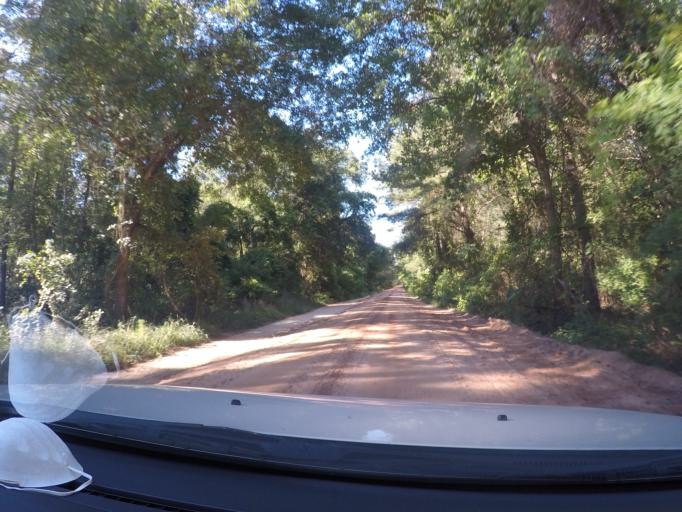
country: US
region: Georgia
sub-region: Bulloch County
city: Brooklet
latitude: 32.2987
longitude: -81.7504
